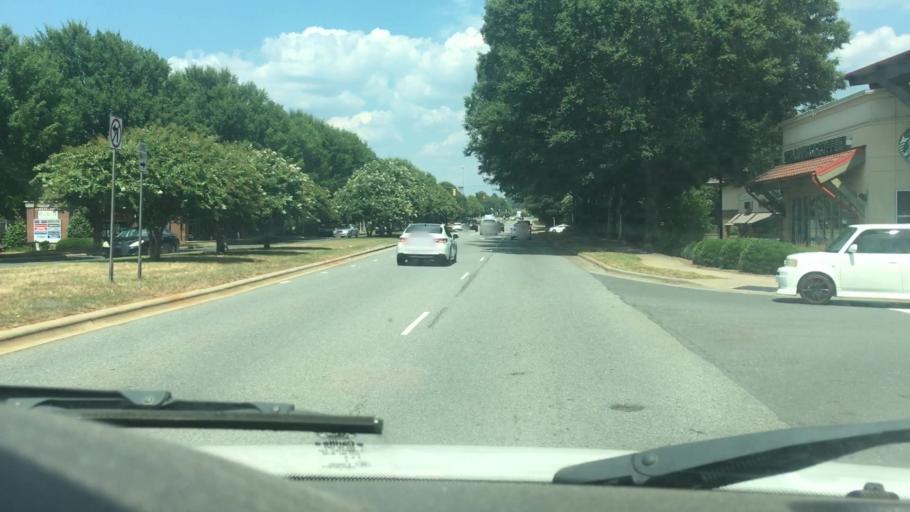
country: US
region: North Carolina
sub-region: Mecklenburg County
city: Huntersville
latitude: 35.4065
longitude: -80.8642
